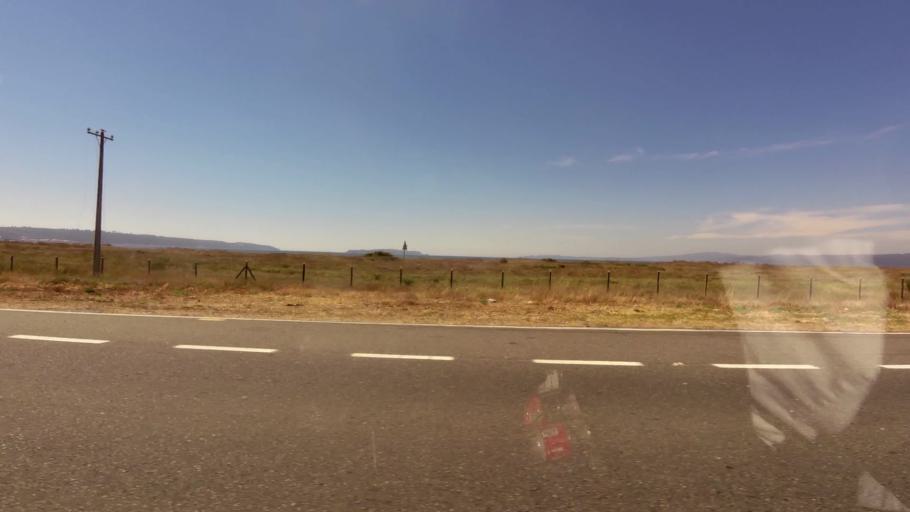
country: CL
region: Biobio
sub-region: Provincia de Concepcion
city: Talcahuano
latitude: -36.7340
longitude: -73.0670
